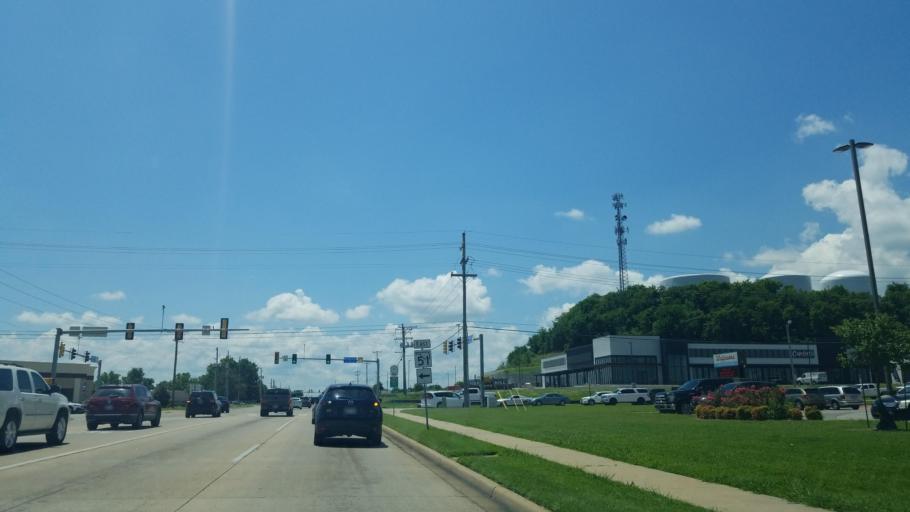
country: US
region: Oklahoma
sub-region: Tulsa County
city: Broken Arrow
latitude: 36.0617
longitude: -95.7797
